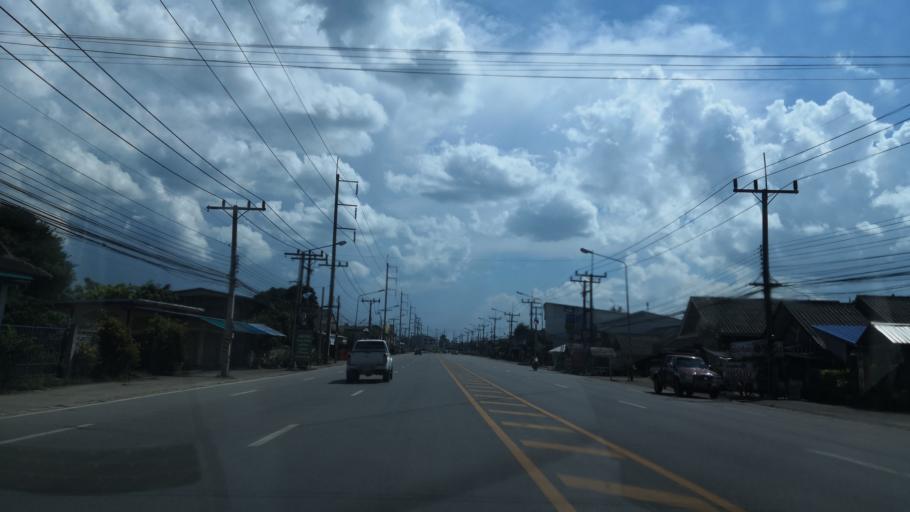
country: TH
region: Chiang Rai
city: Mae Suai
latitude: 19.5777
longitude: 99.4928
